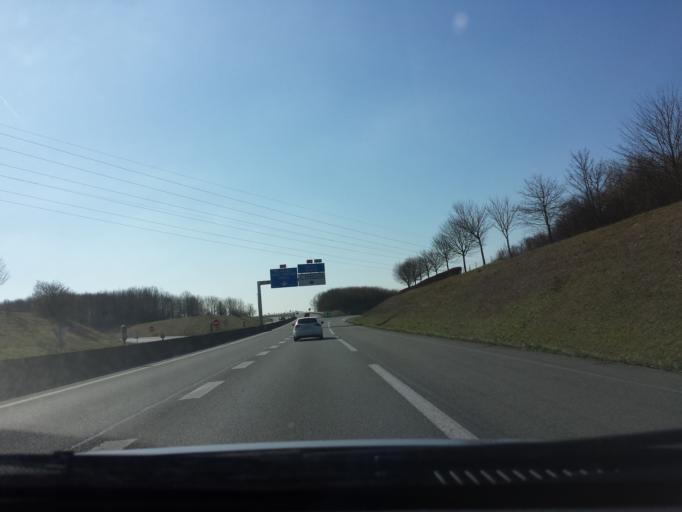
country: FR
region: Picardie
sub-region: Departement de la Somme
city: Saleux
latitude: 49.8500
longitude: 2.2425
